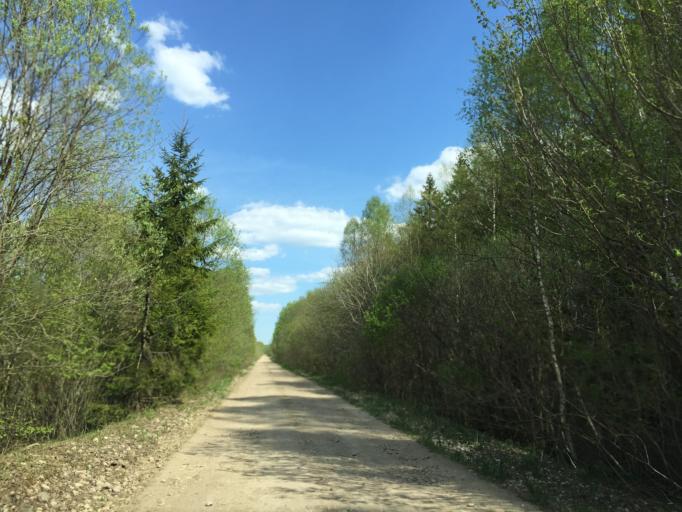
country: LV
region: Limbazu Rajons
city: Limbazi
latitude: 57.4048
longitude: 24.6046
